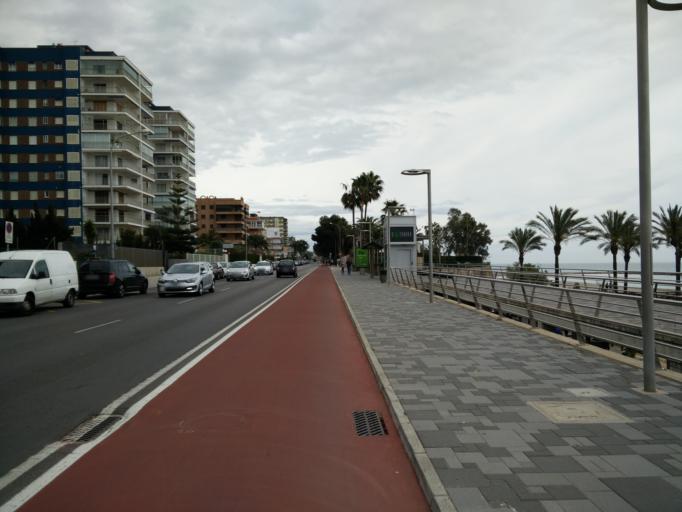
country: ES
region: Valencia
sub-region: Provincia de Castello
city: Benicassim
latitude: 40.0392
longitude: 0.0540
